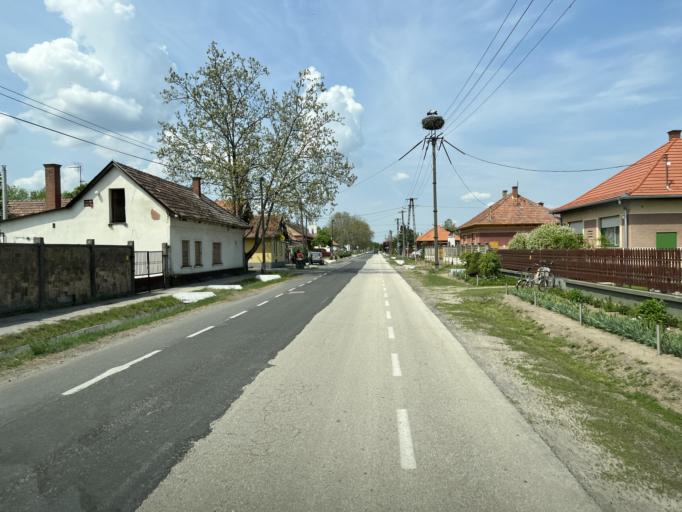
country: HU
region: Pest
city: Cegled
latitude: 47.1019
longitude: 19.7997
